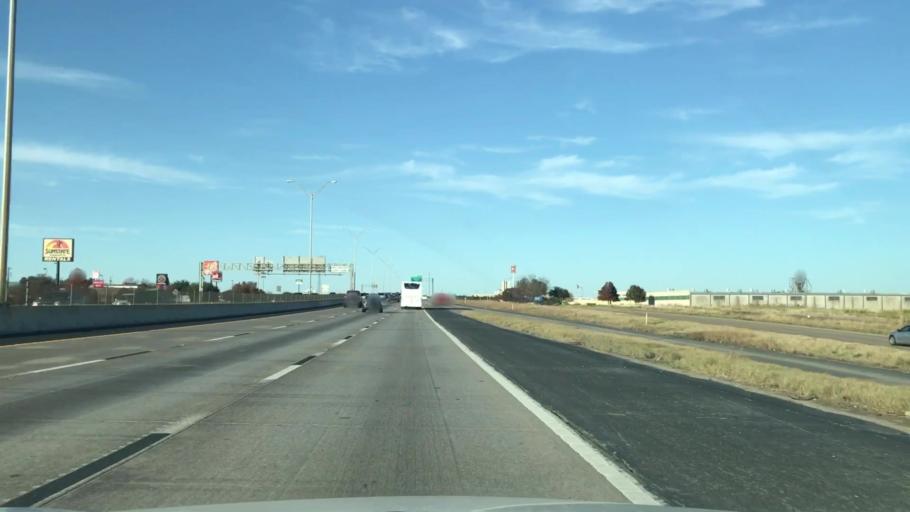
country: US
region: Texas
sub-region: Tarrant County
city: Everman
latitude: 32.6303
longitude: -97.3214
